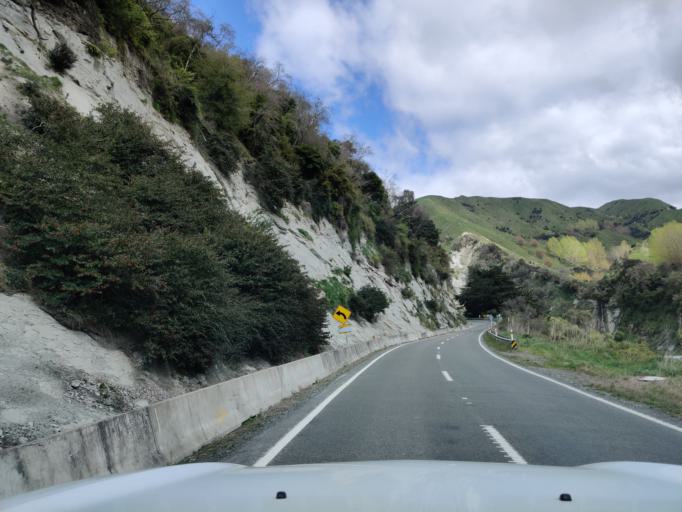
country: NZ
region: Manawatu-Wanganui
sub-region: Ruapehu District
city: Waiouru
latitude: -39.6463
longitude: 175.3260
